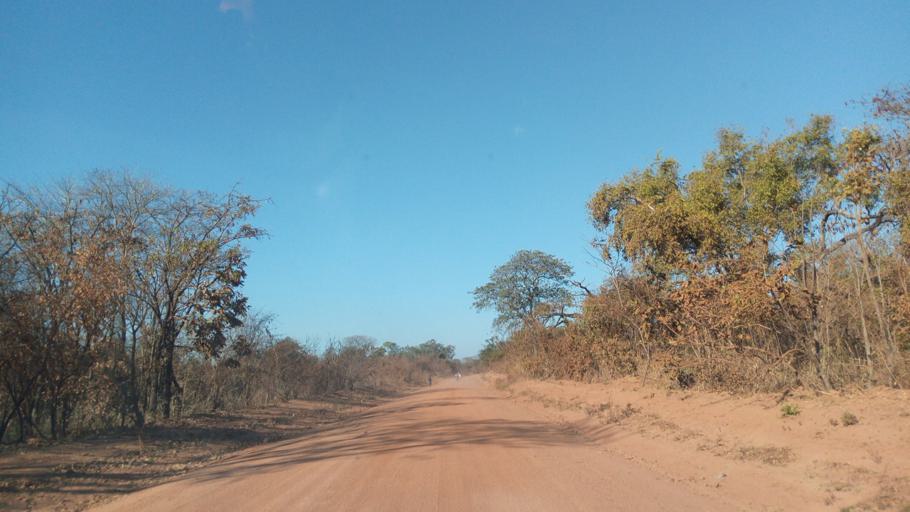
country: ZM
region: Luapula
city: Mwense
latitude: -10.5292
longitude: 28.4541
